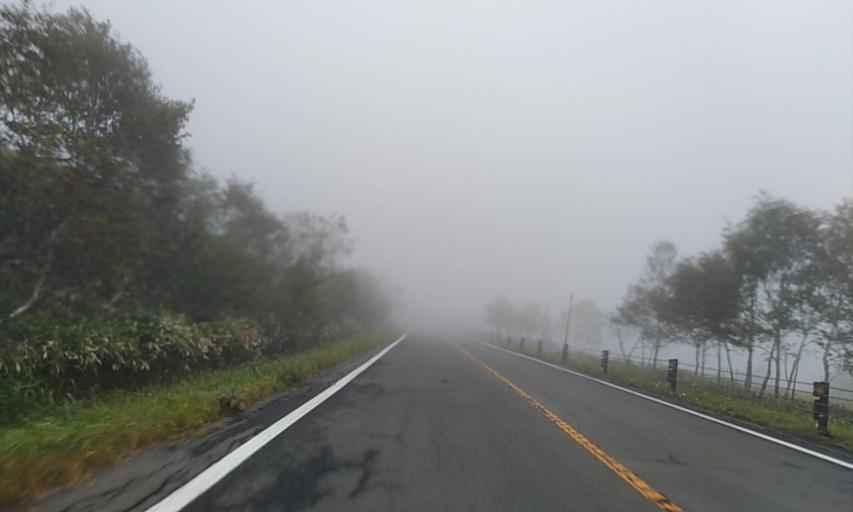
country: JP
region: Hokkaido
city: Bihoro
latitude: 43.5487
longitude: 144.5035
